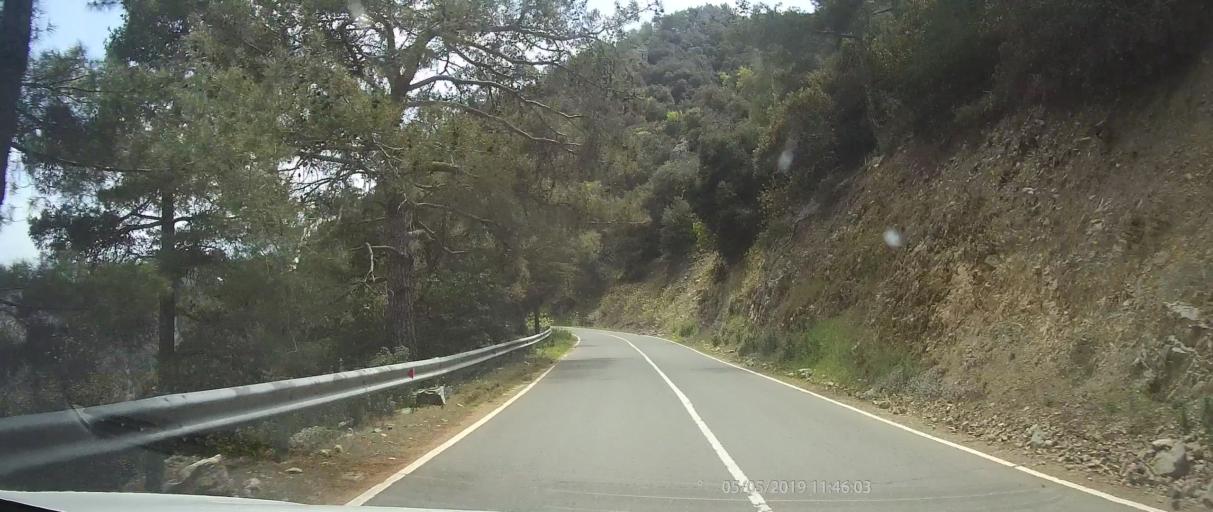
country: CY
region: Lefkosia
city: Kato Pyrgos
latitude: 35.0118
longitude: 32.6809
